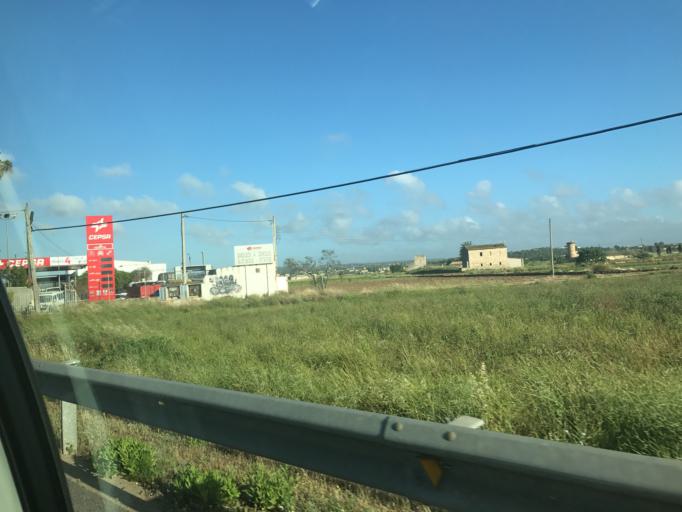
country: ES
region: Balearic Islands
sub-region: Illes Balears
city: s'Arenal
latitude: 39.5477
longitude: 2.7555
